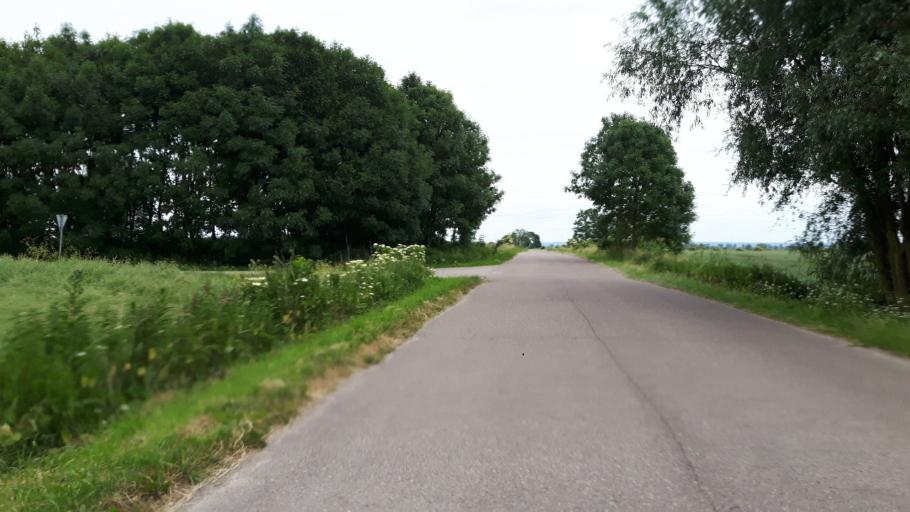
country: PL
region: Pomeranian Voivodeship
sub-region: Powiat nowodworski
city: Sztutowo
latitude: 54.2688
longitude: 19.1851
